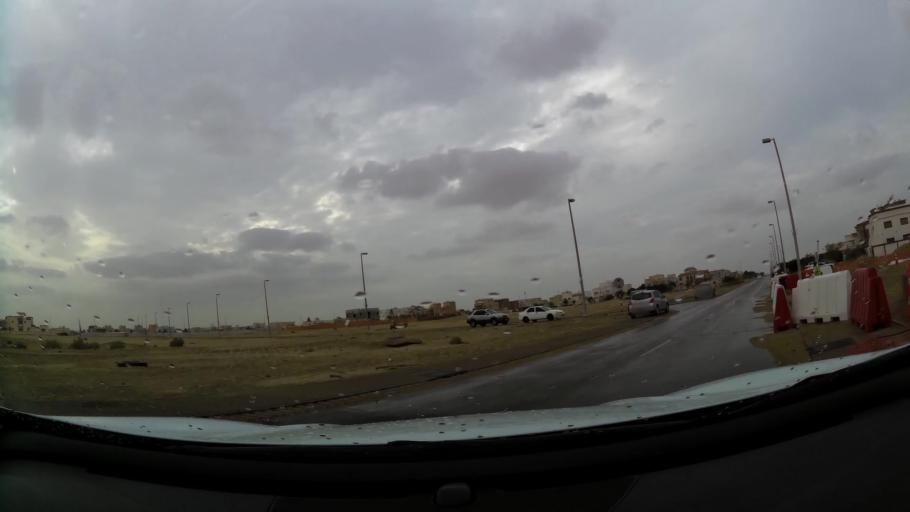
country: AE
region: Abu Dhabi
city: Abu Dhabi
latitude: 24.3576
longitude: 54.6264
